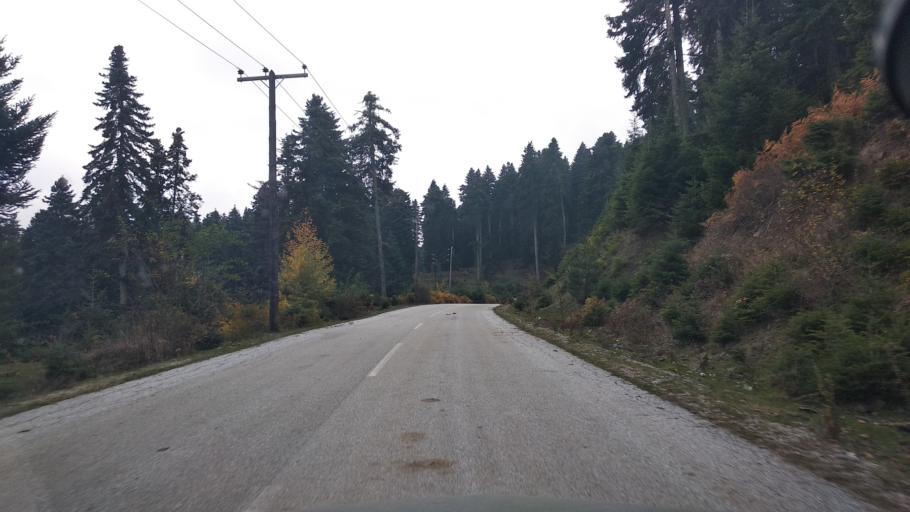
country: GR
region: Thessaly
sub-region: Trikala
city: Pyli
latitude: 39.5779
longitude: 21.4927
